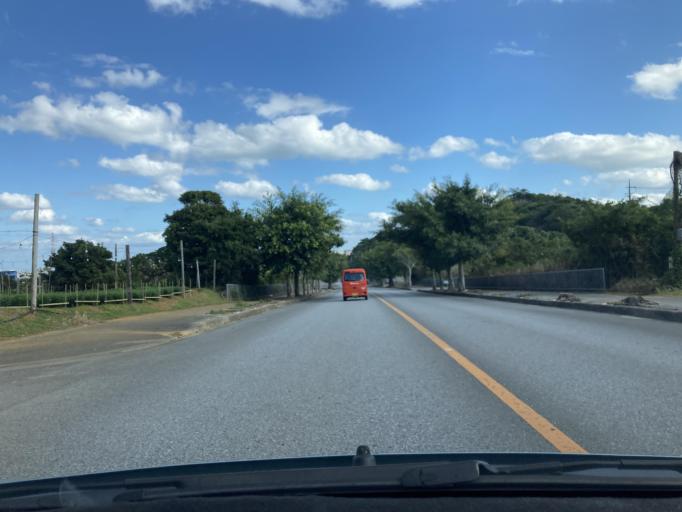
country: JP
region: Okinawa
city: Gushikawa
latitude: 26.3690
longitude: 127.8335
